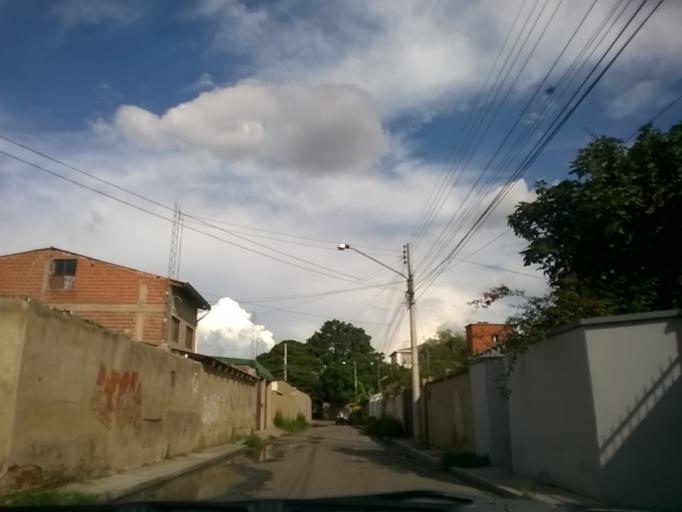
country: BO
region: Cochabamba
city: Cochabamba
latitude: -17.3648
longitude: -66.1838
